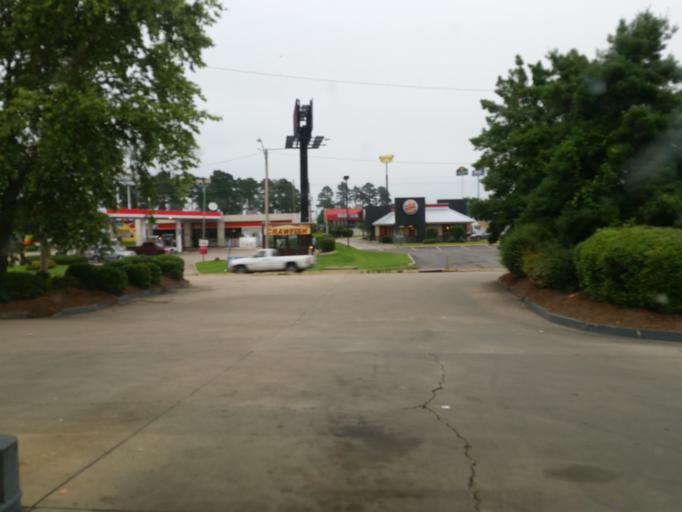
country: US
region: Louisiana
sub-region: Caddo Parish
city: Greenwood
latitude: 32.4472
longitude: -93.8650
